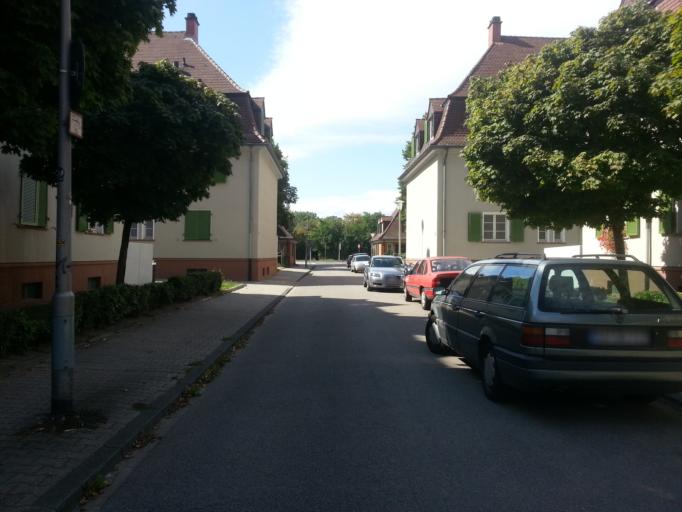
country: DE
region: Baden-Wuerttemberg
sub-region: Karlsruhe Region
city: Mannheim
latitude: 49.5026
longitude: 8.4889
